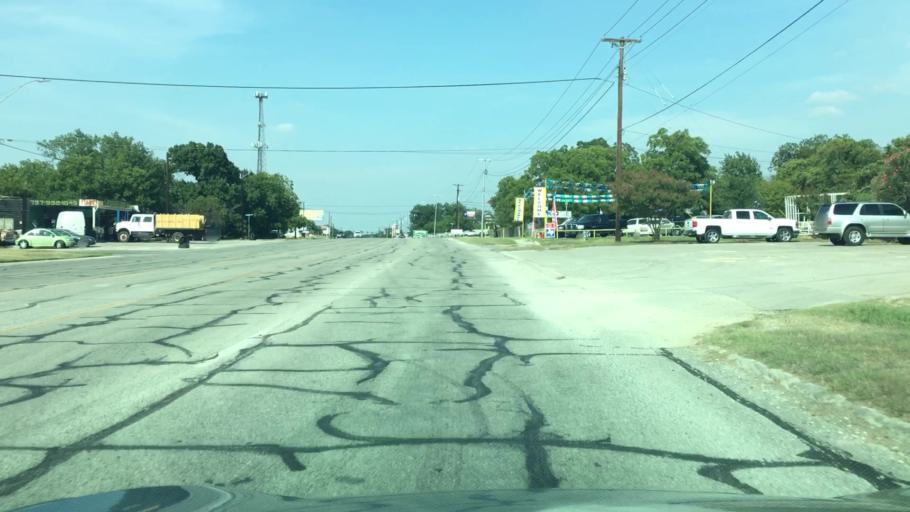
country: US
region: Texas
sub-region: Comal County
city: New Braunfels
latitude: 29.6863
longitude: -98.1334
